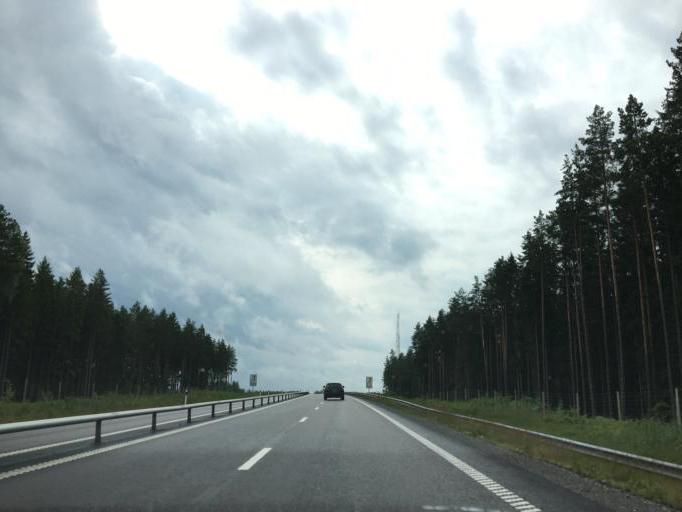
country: SE
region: Soedermanland
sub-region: Katrineholms Kommun
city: Katrineholm
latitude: 59.0032
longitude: 16.2466
